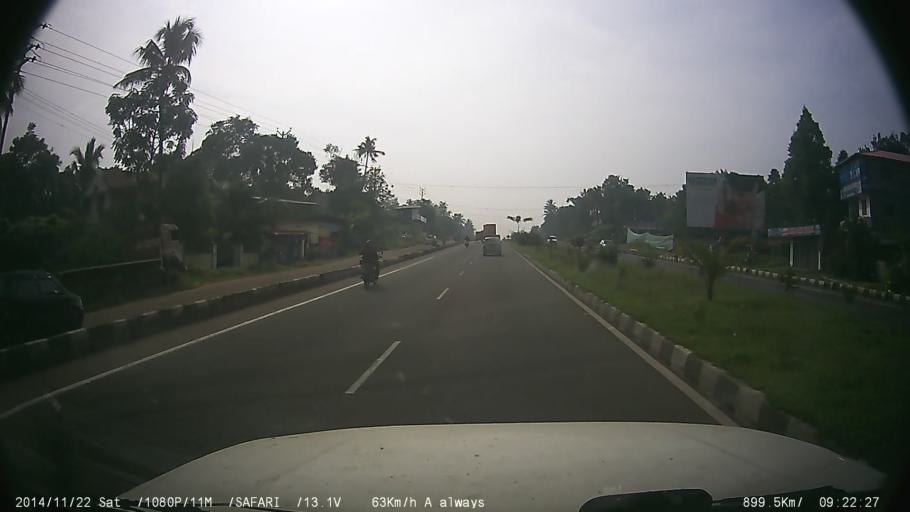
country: IN
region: Kerala
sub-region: Ernakulam
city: Angamali
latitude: 10.2165
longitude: 76.3783
